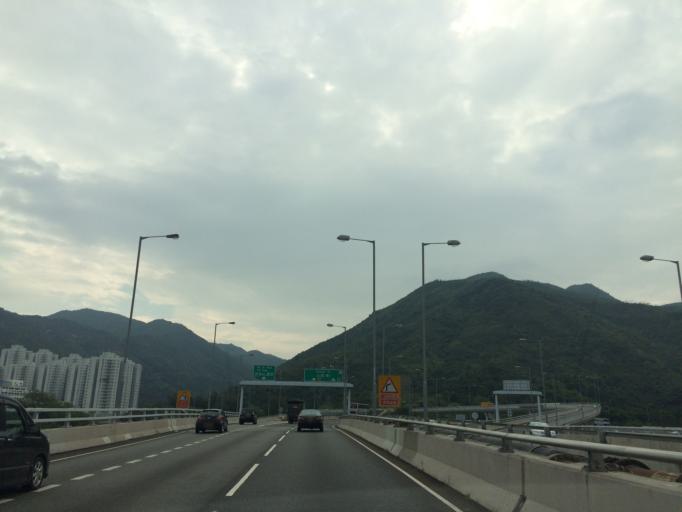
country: HK
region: Sha Tin
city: Sha Tin
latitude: 22.4068
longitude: 114.2170
